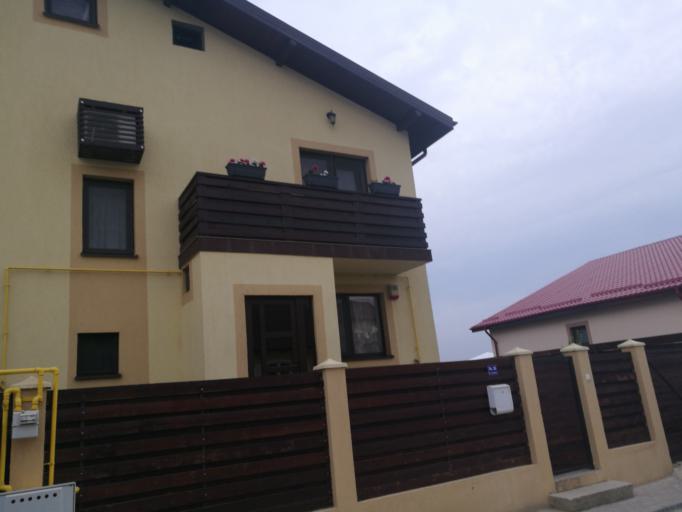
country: RO
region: Ilfov
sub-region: Comuna Vidra
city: Vidra
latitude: 44.2769
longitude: 26.1843
